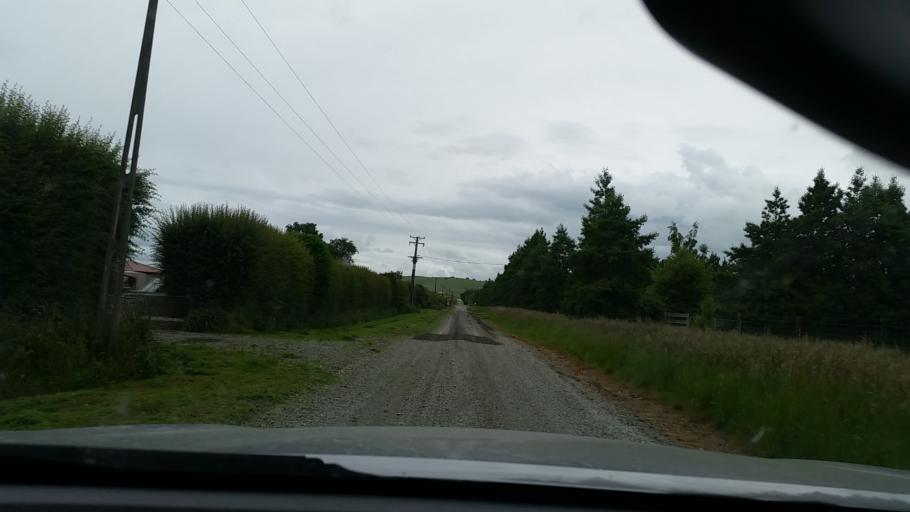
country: NZ
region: Southland
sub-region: Southland District
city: Winton
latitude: -46.0995
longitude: 168.3250
